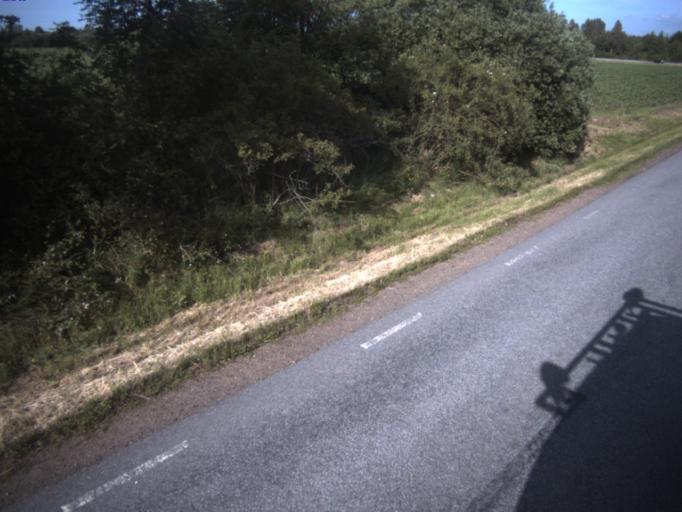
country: SE
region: Skane
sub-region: Helsingborg
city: Odakra
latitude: 56.0808
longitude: 12.7613
